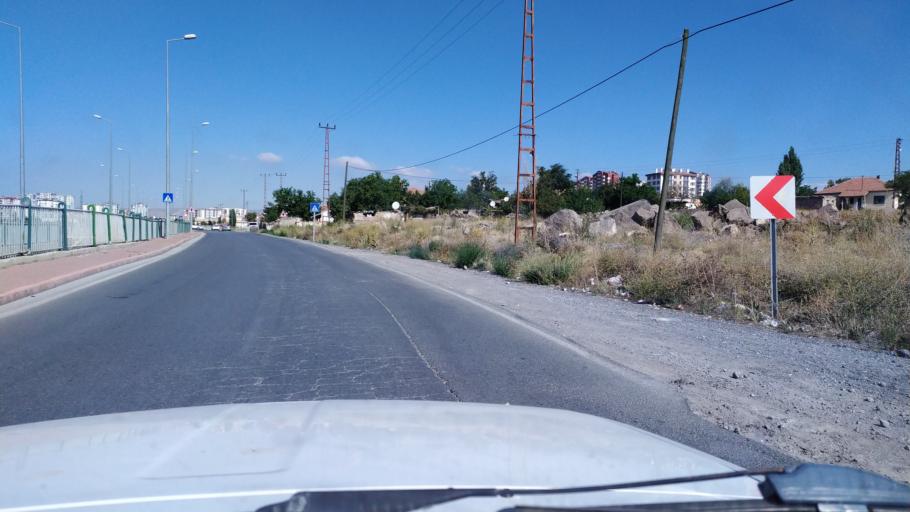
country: TR
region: Kayseri
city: Talas
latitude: 38.7330
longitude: 35.5490
